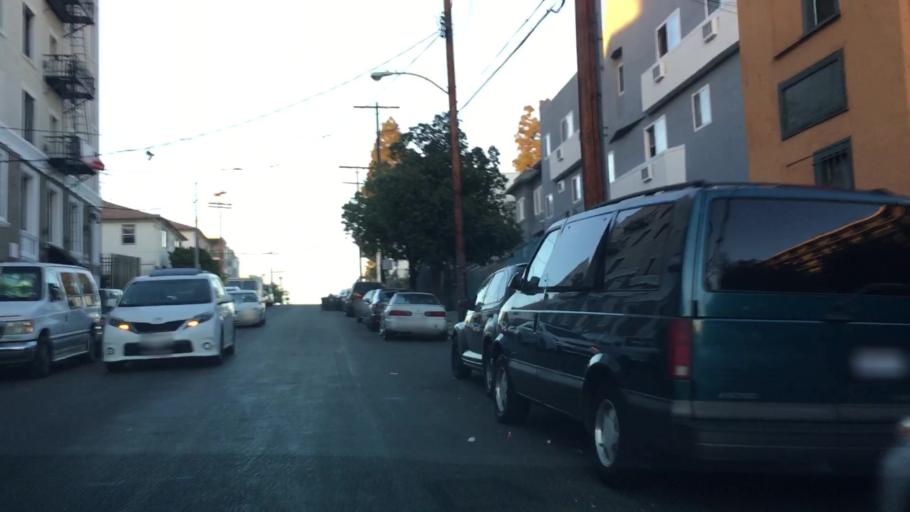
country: US
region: California
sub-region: Los Angeles County
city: Echo Park
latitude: 34.0619
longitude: -118.2761
